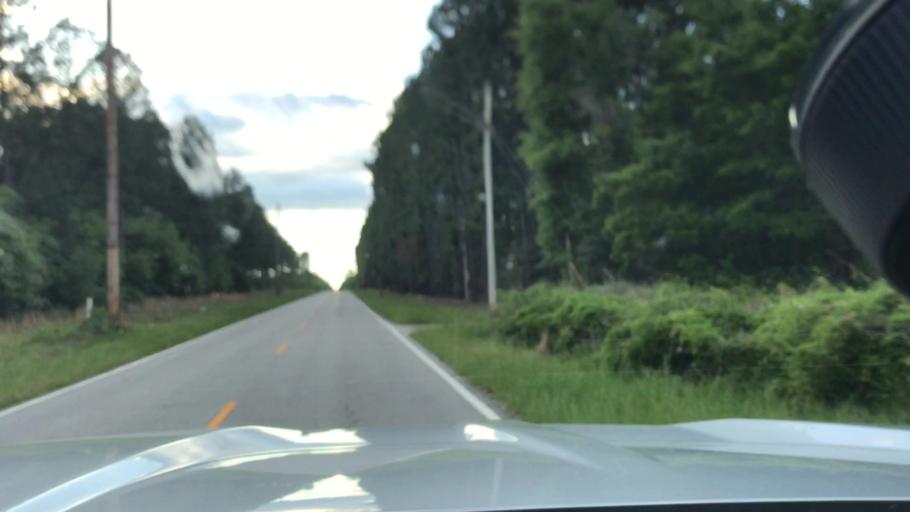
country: US
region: South Carolina
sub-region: Bamberg County
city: Denmark
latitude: 33.4597
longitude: -81.1490
